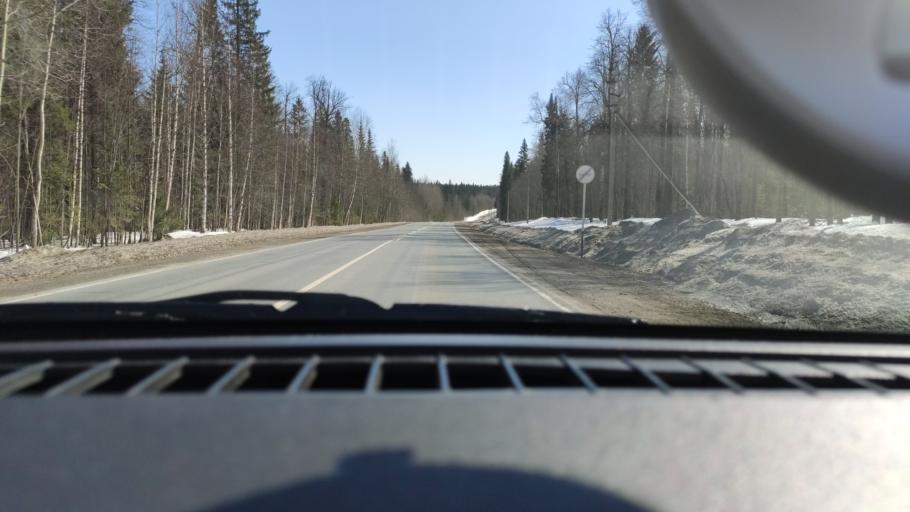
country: RU
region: Perm
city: Perm
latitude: 58.2072
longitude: 56.1955
